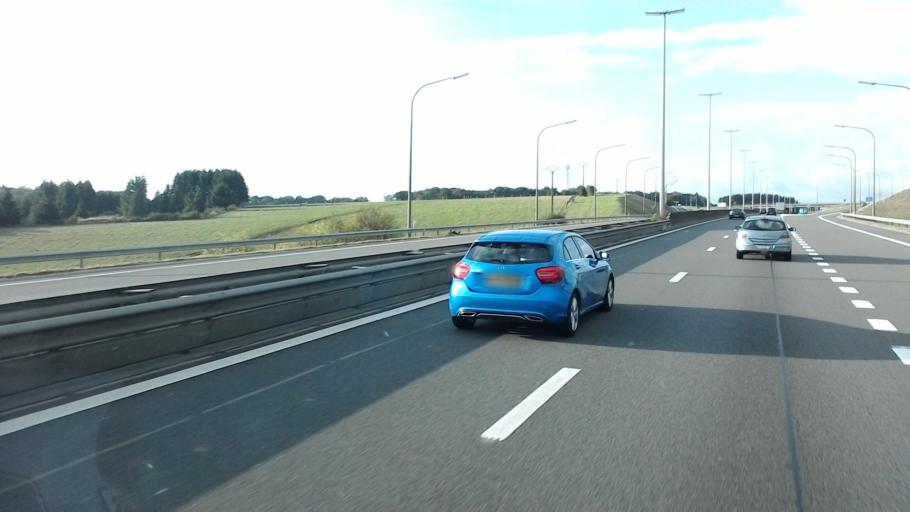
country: BE
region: Wallonia
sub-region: Province du Luxembourg
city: Leglise
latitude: 49.8032
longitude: 5.5201
